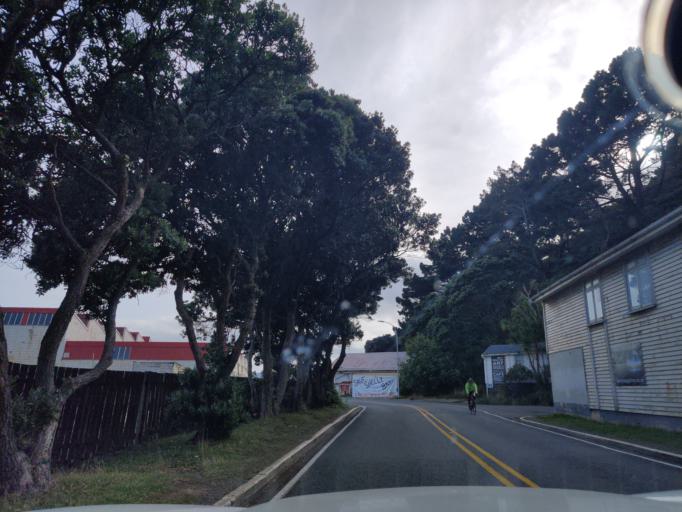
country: NZ
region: Wellington
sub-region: Wellington City
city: Wellington
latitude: -41.2950
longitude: 174.8221
